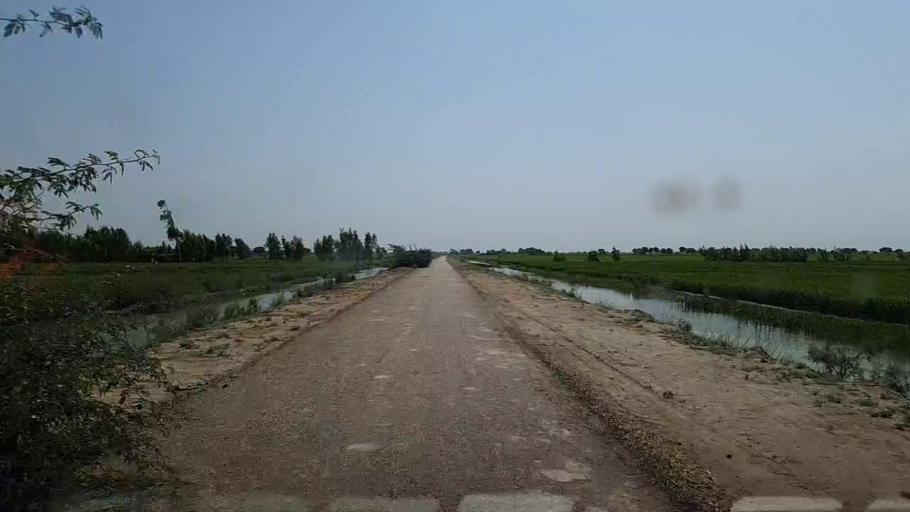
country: PK
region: Sindh
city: Mirpur Batoro
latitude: 24.6109
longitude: 68.4523
